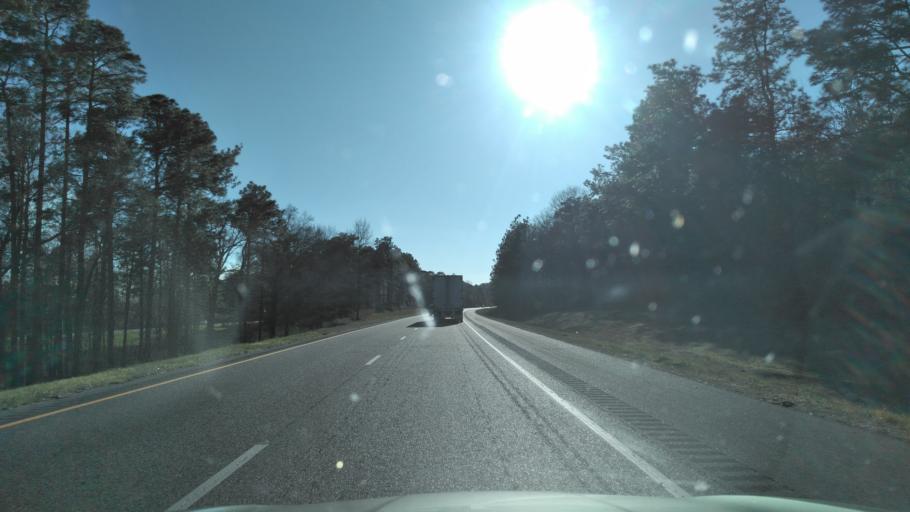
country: US
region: Alabama
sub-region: Escambia County
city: Atmore
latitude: 31.0675
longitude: -87.5590
